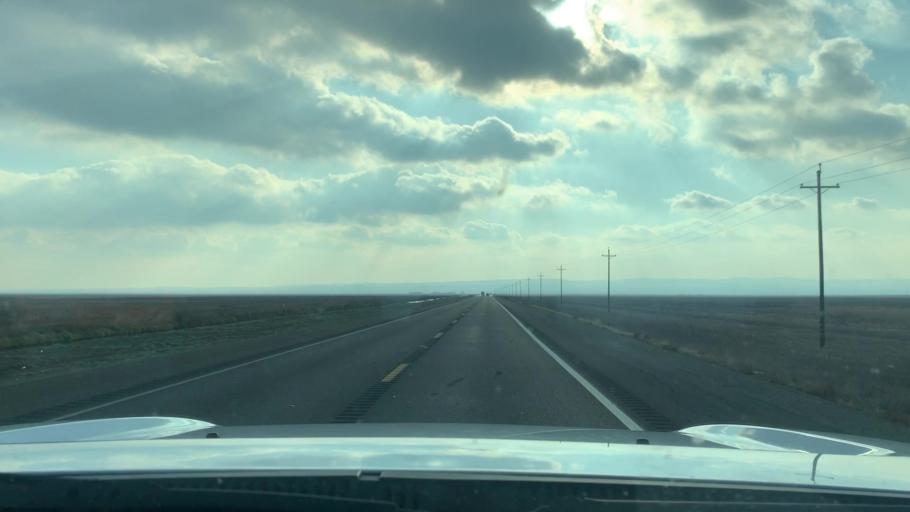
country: US
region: California
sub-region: Kings County
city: Kettleman City
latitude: 36.0873
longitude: -119.9149
